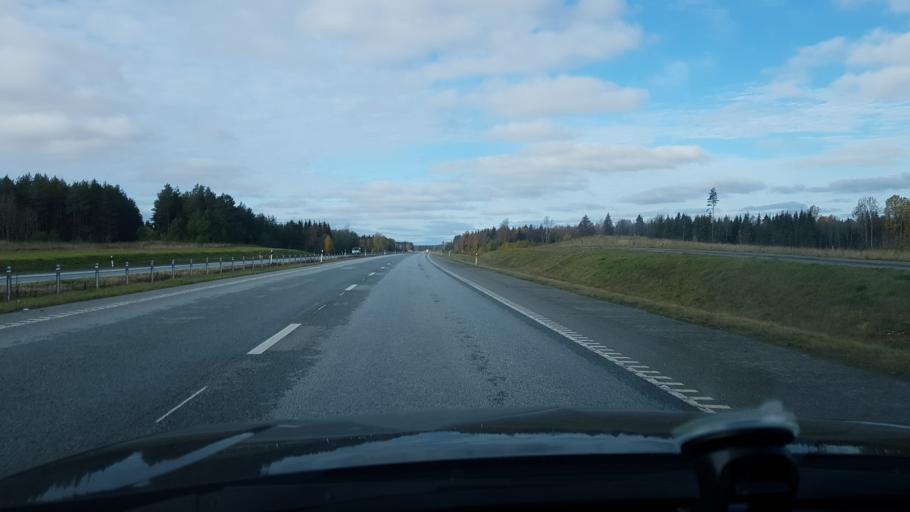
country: EE
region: Laeaene-Virumaa
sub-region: Kadrina vald
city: Kadrina
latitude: 59.4511
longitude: 26.0650
